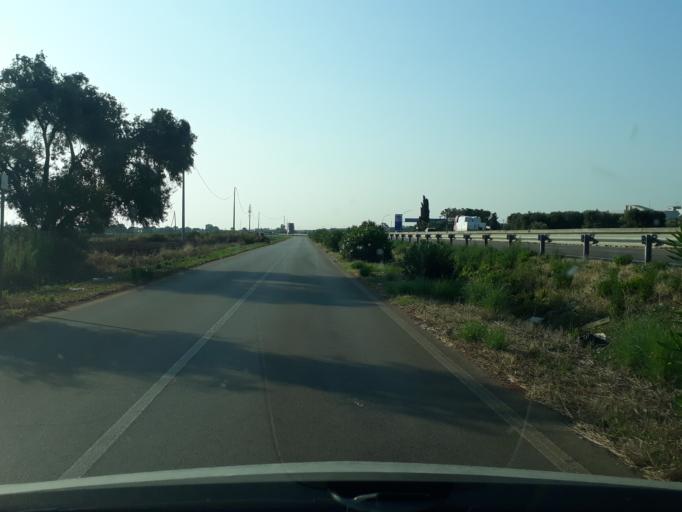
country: IT
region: Apulia
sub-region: Provincia di Brindisi
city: Carovigno
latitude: 40.7377
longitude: 17.7230
